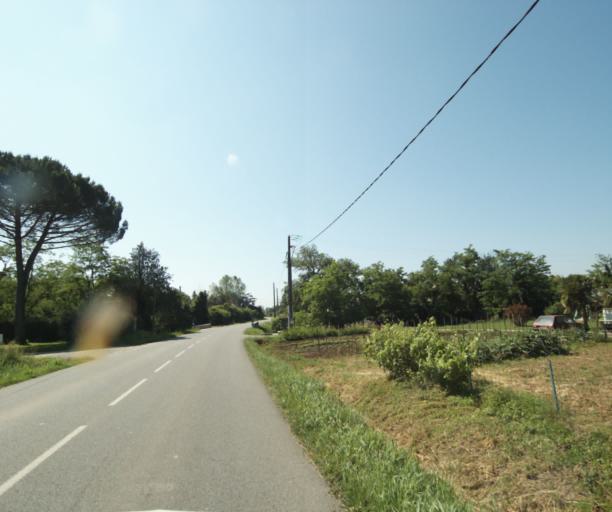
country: FR
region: Midi-Pyrenees
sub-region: Departement du Tarn-et-Garonne
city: Montbeton
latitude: 44.0275
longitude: 1.3147
